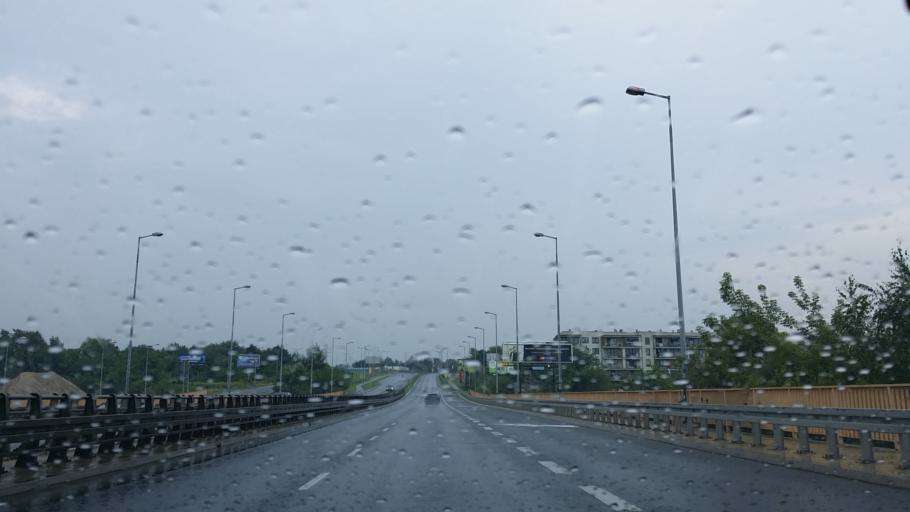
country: PL
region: Lesser Poland Voivodeship
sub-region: Krakow
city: Krakow
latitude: 50.0271
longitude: 19.9447
